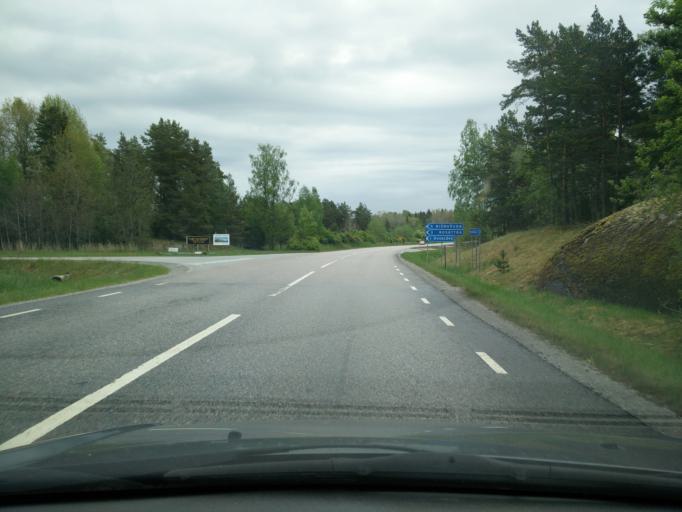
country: SE
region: Stockholm
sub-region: Norrtalje Kommun
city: Bjorko
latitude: 59.8202
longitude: 18.9026
